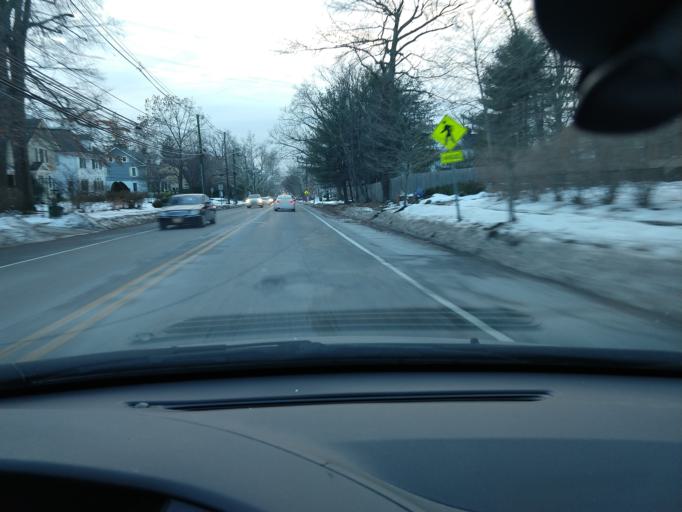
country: US
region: New Jersey
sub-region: Middlesex County
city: Metuchen
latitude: 40.5469
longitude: -74.3581
